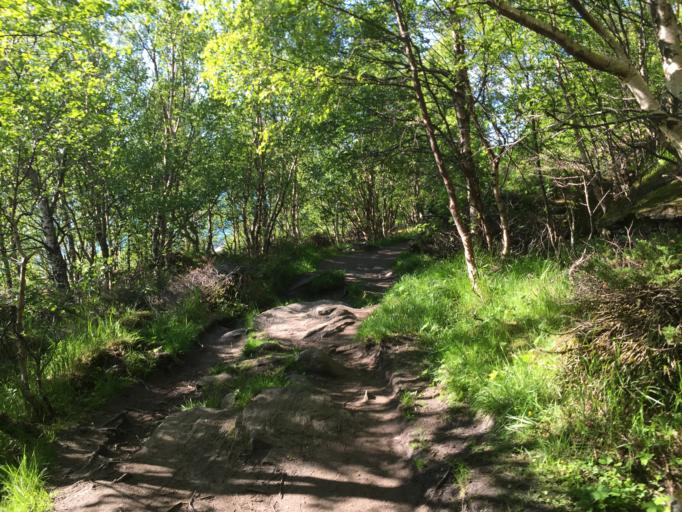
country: NO
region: Nordland
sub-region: Bodo
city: Loding
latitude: 67.4166
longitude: 14.6325
